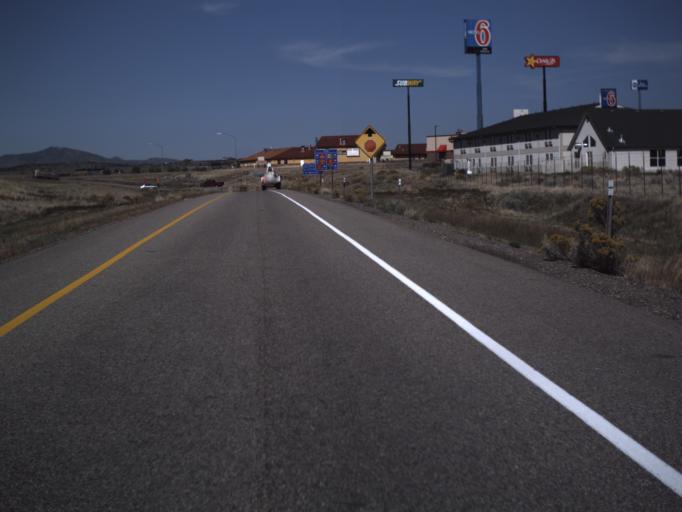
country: US
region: Utah
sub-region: Beaver County
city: Beaver
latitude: 38.2906
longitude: -112.6503
